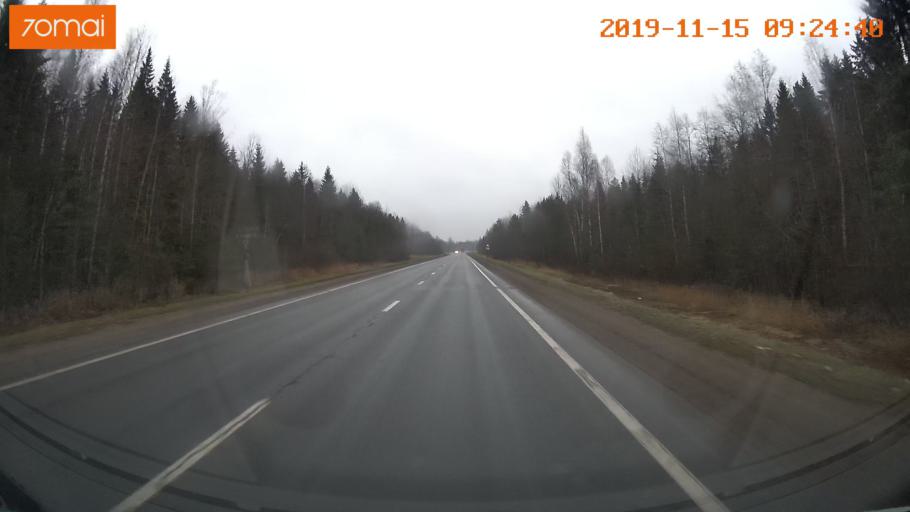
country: RU
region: Vologda
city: Tonshalovo
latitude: 59.3052
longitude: 38.1450
